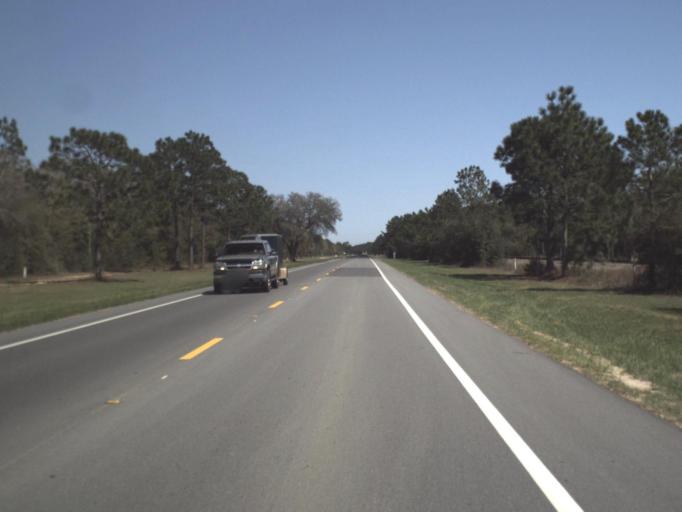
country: US
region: Florida
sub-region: Walton County
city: DeFuniak Springs
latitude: 30.7515
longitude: -86.2788
